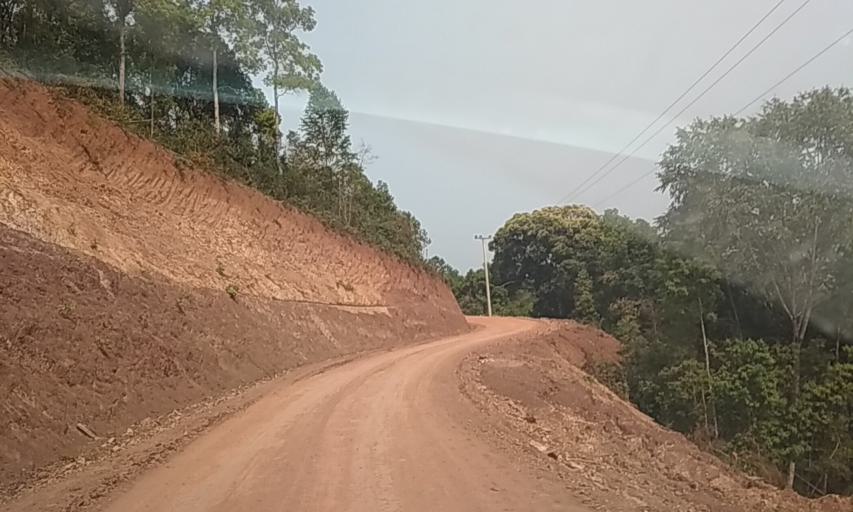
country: VN
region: Huyen Dien Bien
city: Dien Bien Phu
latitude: 21.4609
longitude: 102.7726
